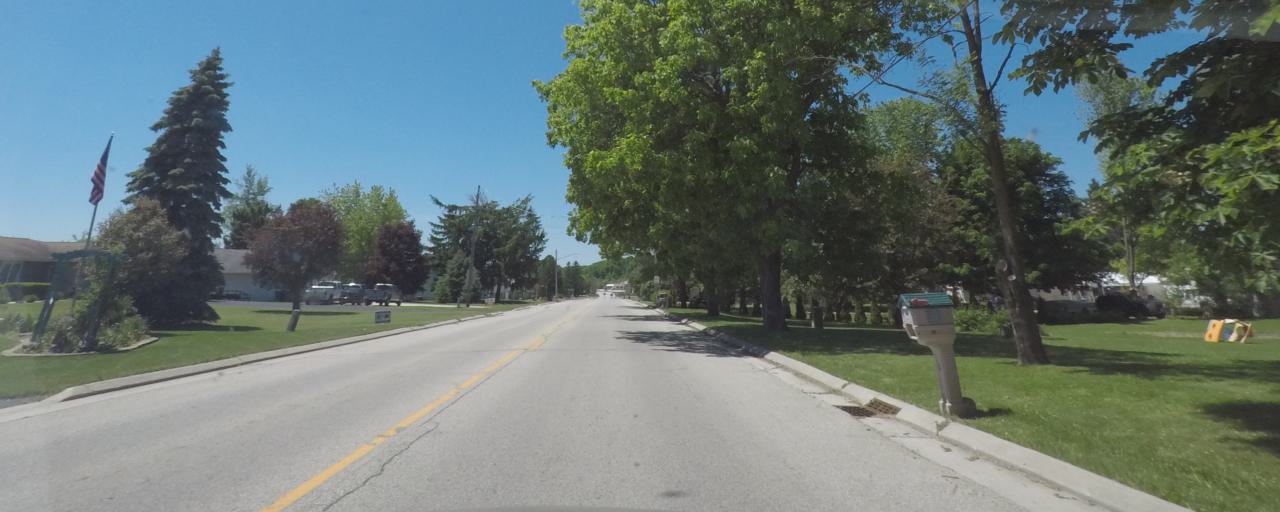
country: US
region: Wisconsin
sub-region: Sheboygan County
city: Plymouth
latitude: 43.6553
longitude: -88.0139
